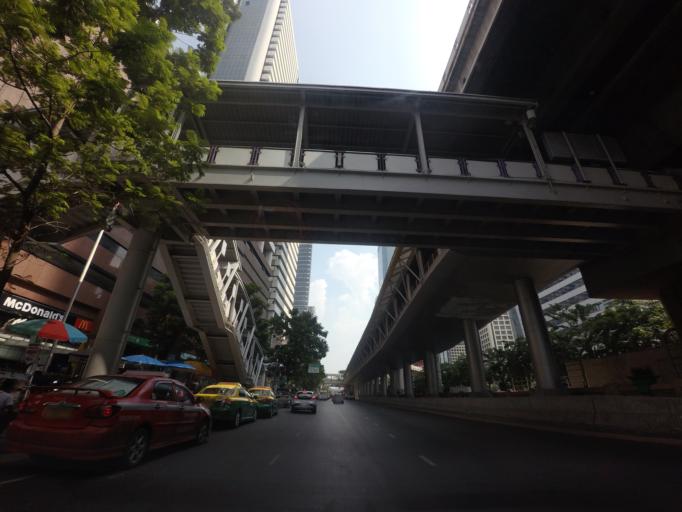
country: TH
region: Bangkok
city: Bang Rak
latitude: 13.7234
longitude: 100.5296
